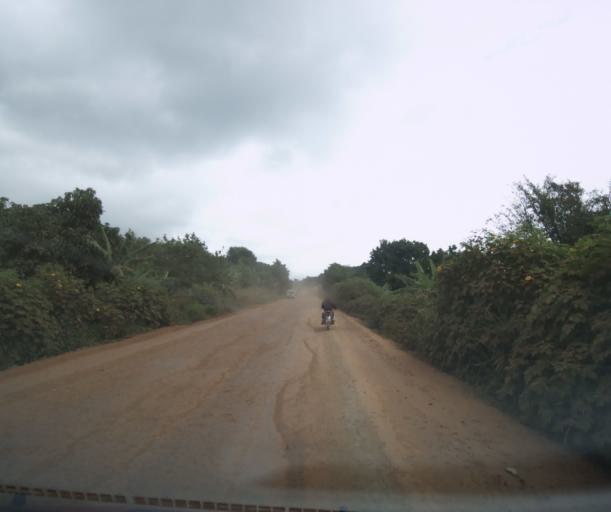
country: CM
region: West
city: Mbouda
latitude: 5.6730
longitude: 10.2138
